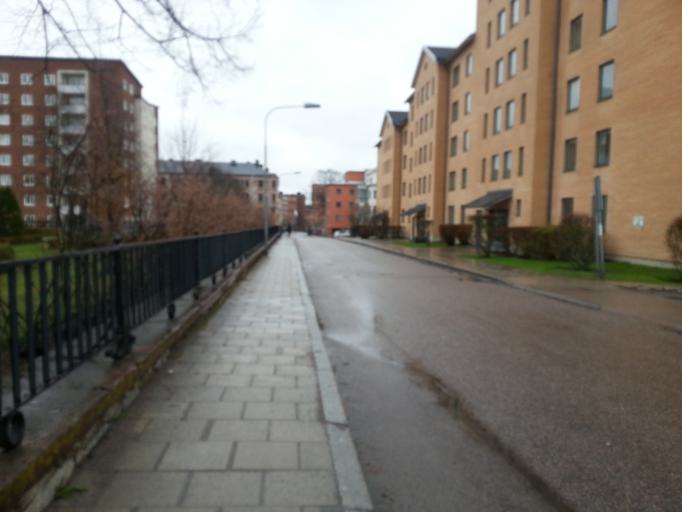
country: SE
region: OEstergoetland
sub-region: Norrkopings Kommun
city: Norrkoping
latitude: 58.5900
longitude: 16.1711
